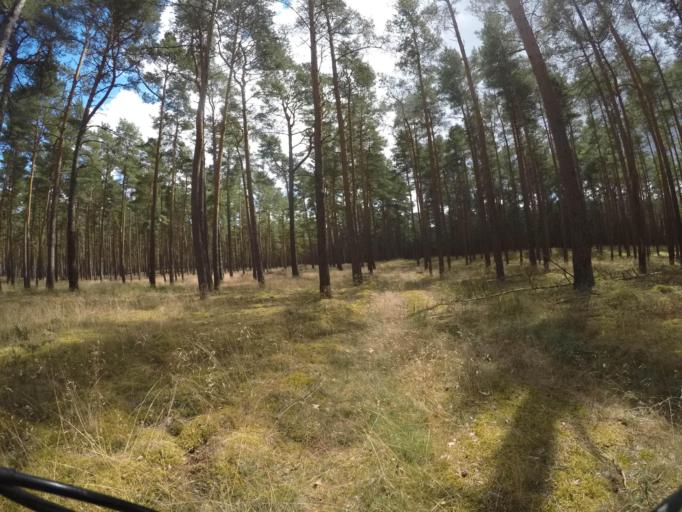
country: DE
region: Lower Saxony
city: Hitzacker
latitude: 53.1929
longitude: 11.0730
